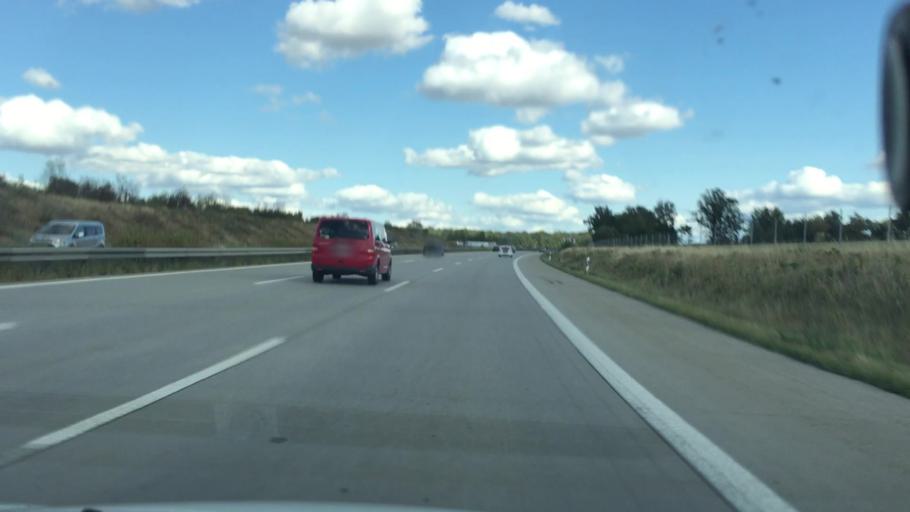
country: DE
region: Saxony
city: Remse
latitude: 50.8437
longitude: 12.5756
